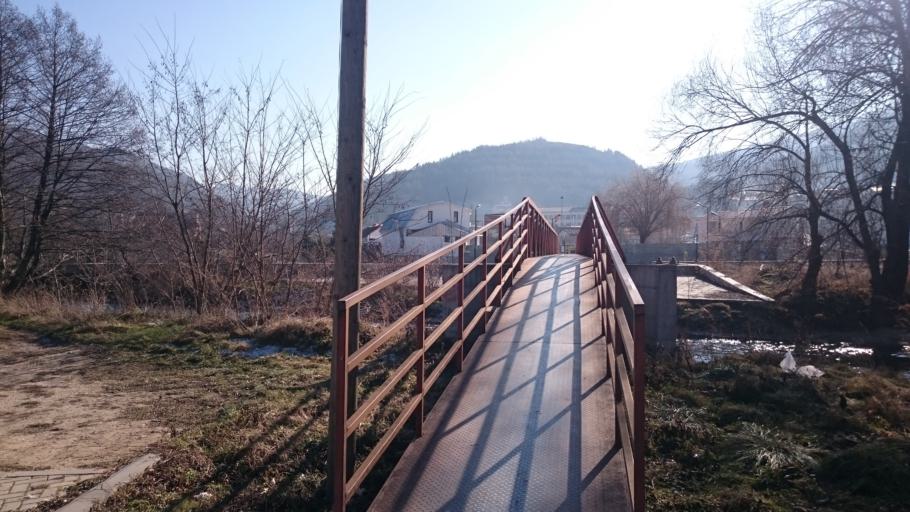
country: MK
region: Makedonski Brod
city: Makedonski Brod
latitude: 41.5108
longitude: 21.2195
